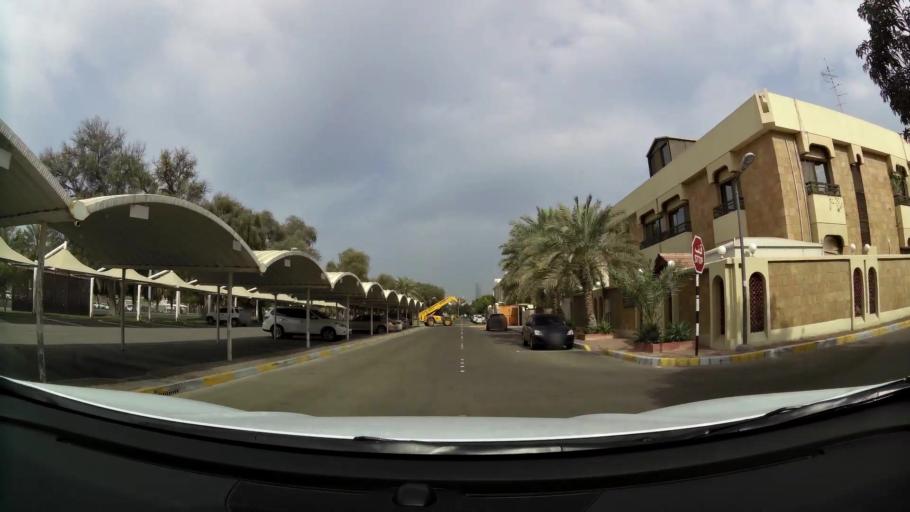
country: AE
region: Abu Dhabi
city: Abu Dhabi
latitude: 24.4555
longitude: 54.3765
